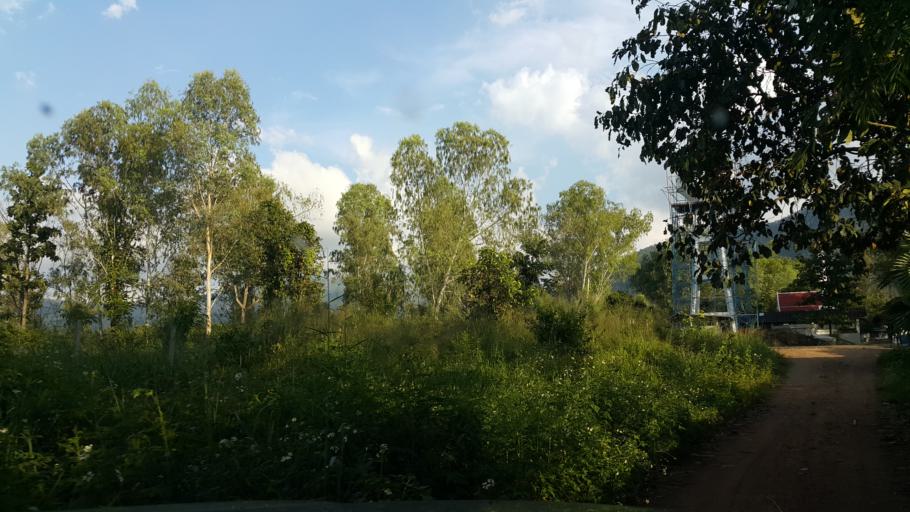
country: TH
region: Chiang Mai
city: Mae On
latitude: 18.7428
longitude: 99.2375
